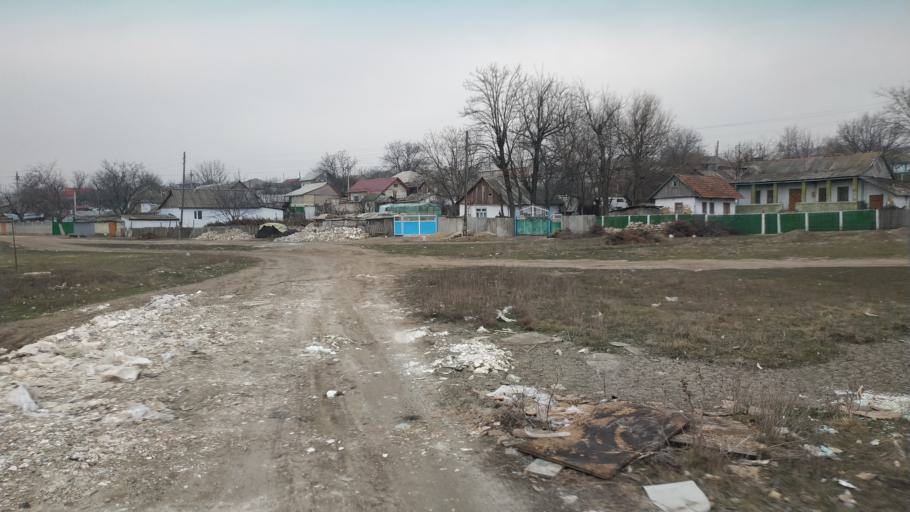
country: MD
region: Chisinau
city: Singera
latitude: 46.8190
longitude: 28.9728
